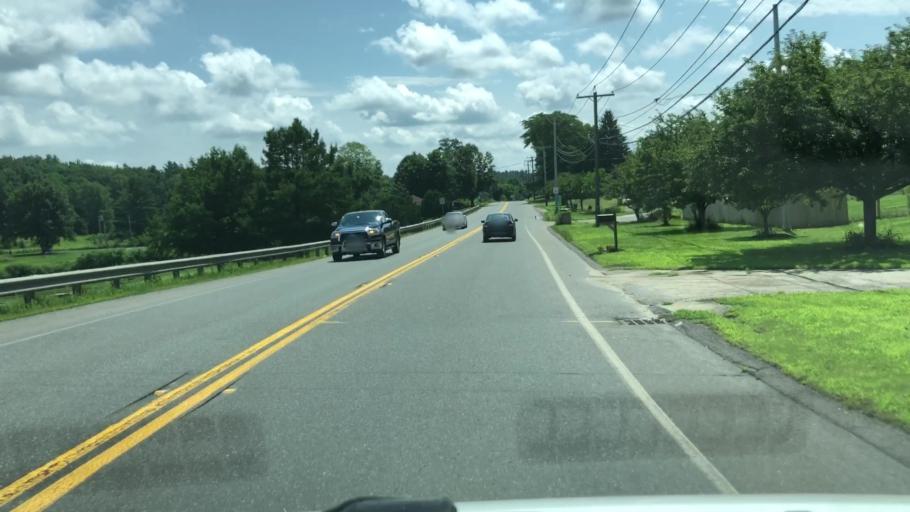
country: US
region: Massachusetts
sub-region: Hampshire County
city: Williamsburg
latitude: 42.3717
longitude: -72.6951
